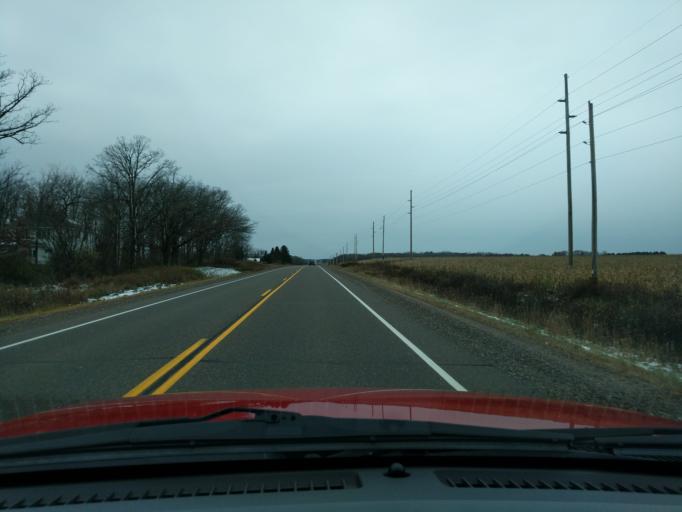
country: US
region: Wisconsin
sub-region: Washburn County
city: Shell Lake
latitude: 45.8153
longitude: -92.0480
